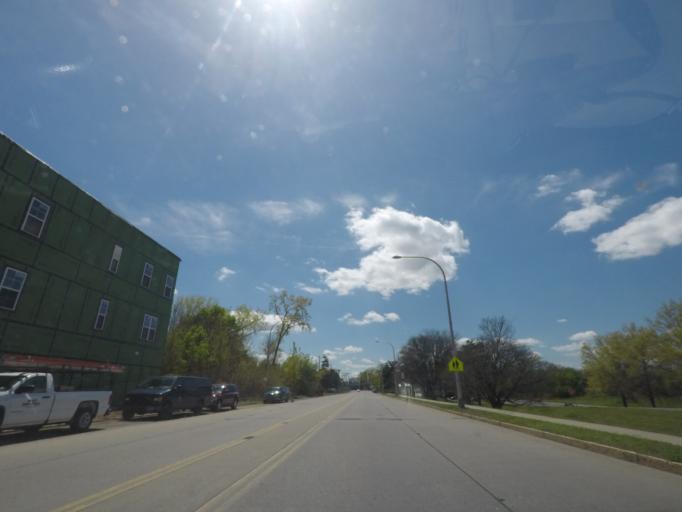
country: US
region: New York
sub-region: Albany County
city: Roessleville
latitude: 42.6735
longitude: -73.8047
